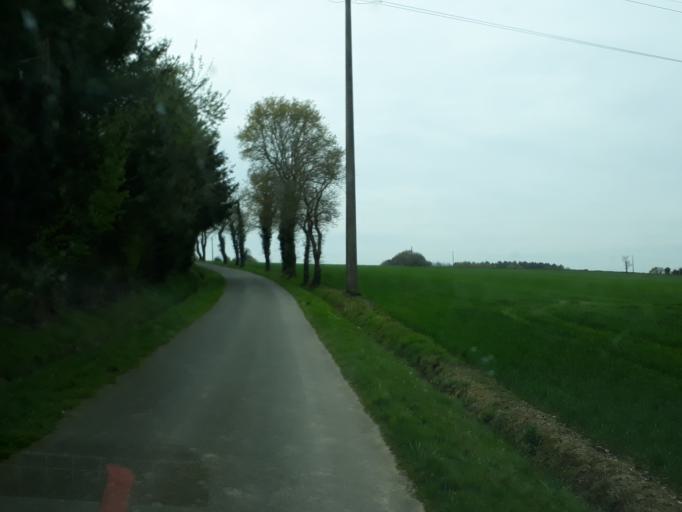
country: FR
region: Brittany
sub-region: Departement du Morbihan
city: Sulniac
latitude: 47.6794
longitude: -2.5890
